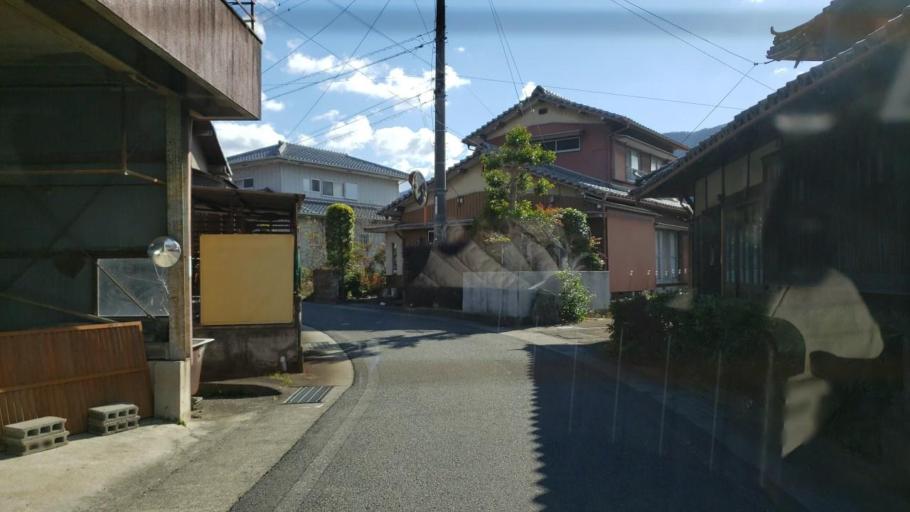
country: JP
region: Tokushima
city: Kamojimacho-jogejima
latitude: 34.0658
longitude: 134.3174
